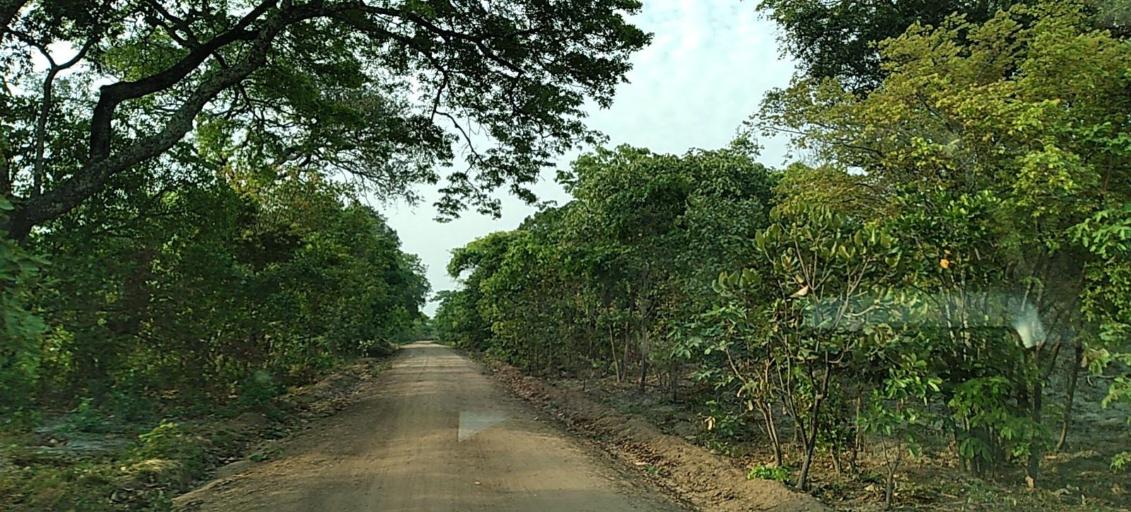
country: ZM
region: Copperbelt
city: Chingola
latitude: -12.8799
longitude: 27.6918
